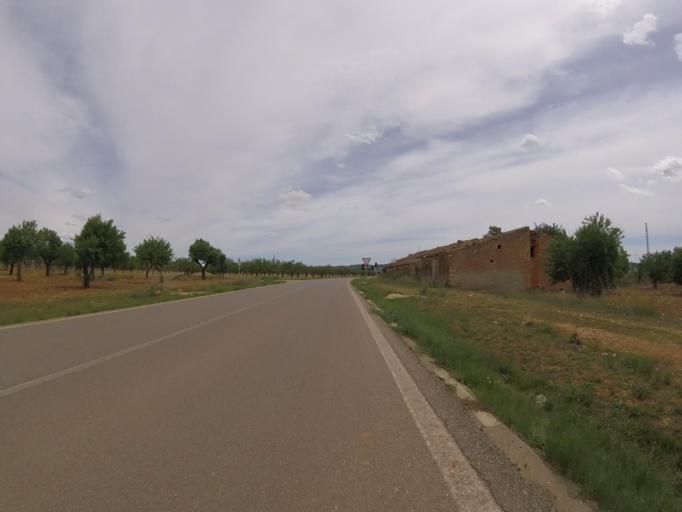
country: ES
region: Valencia
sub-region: Provincia de Castello
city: Cabanes
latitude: 40.1658
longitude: 0.0123
